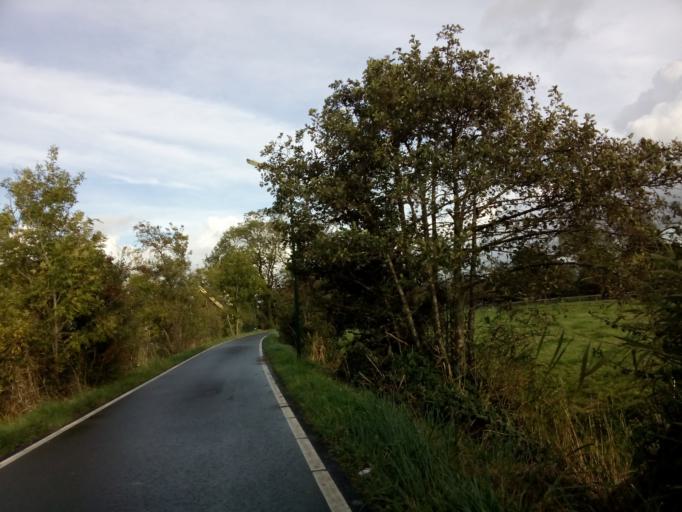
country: NL
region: Utrecht
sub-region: Gemeente Woerden
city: Woerden
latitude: 52.1046
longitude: 4.9276
